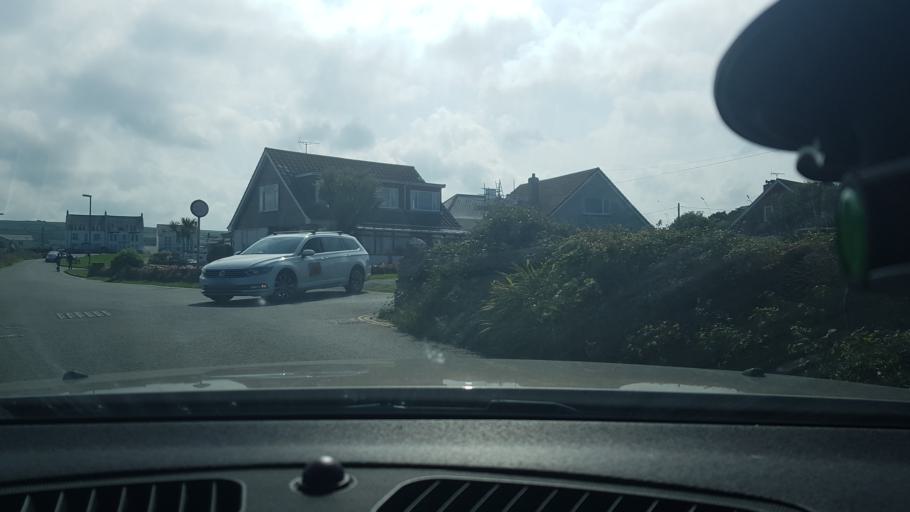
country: GB
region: England
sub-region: Cornwall
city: Tintagel
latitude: 50.6676
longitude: -4.7543
